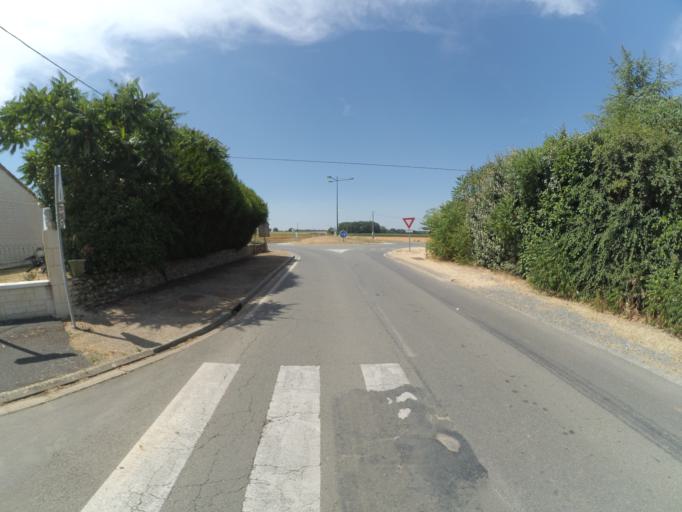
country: FR
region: Poitou-Charentes
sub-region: Departement de la Vienne
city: Vivonne
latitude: 46.4201
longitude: 0.3081
